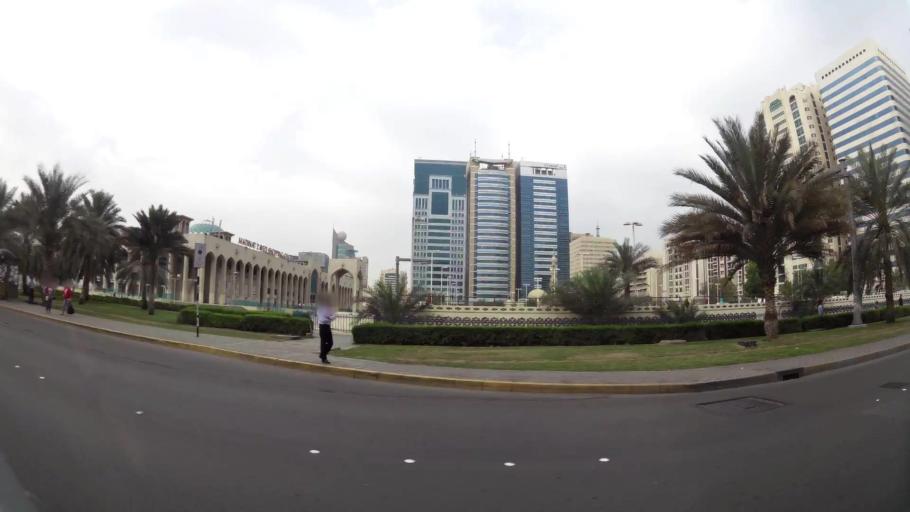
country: AE
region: Abu Dhabi
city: Abu Dhabi
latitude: 24.4861
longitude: 54.3653
